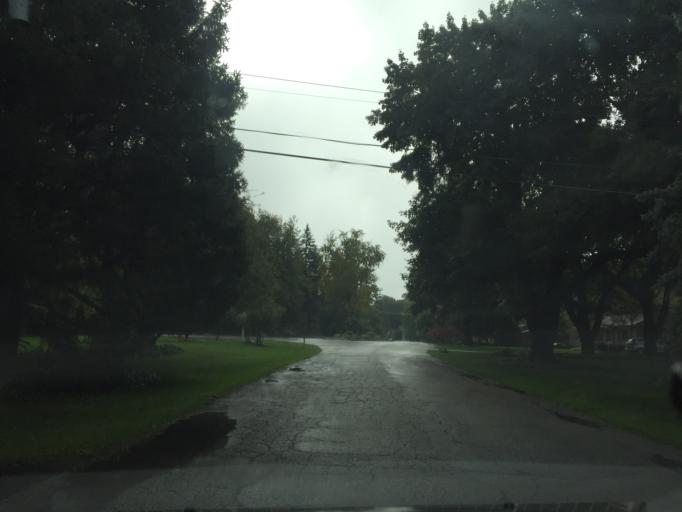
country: US
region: Michigan
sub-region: Oakland County
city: Franklin
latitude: 42.5558
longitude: -83.2890
